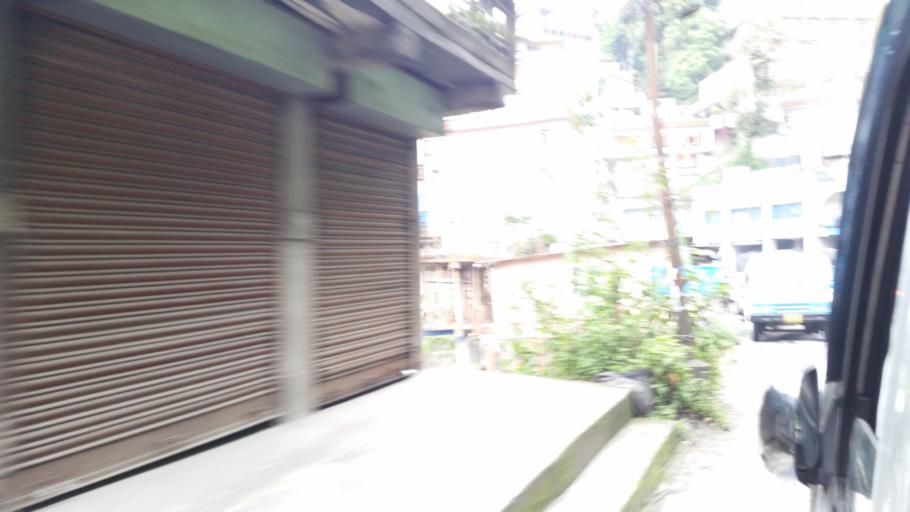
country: IN
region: West Bengal
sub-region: Darjiling
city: Darjiling
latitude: 27.0228
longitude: 88.2546
